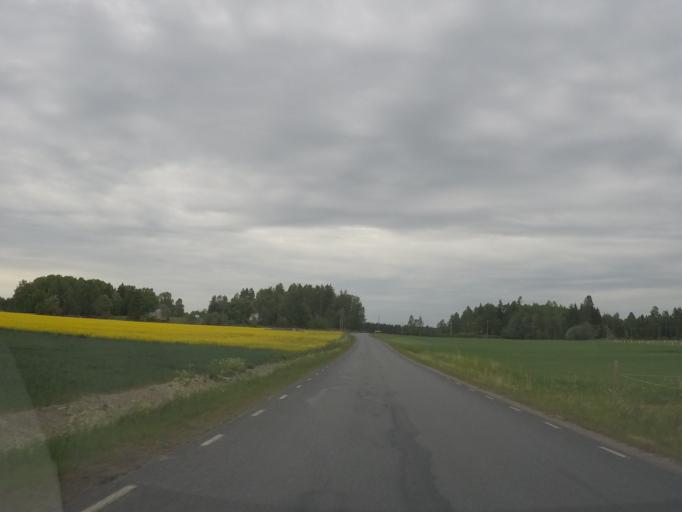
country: SE
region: Soedermanland
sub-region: Eskilstuna Kommun
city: Arla
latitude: 59.2679
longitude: 16.6600
